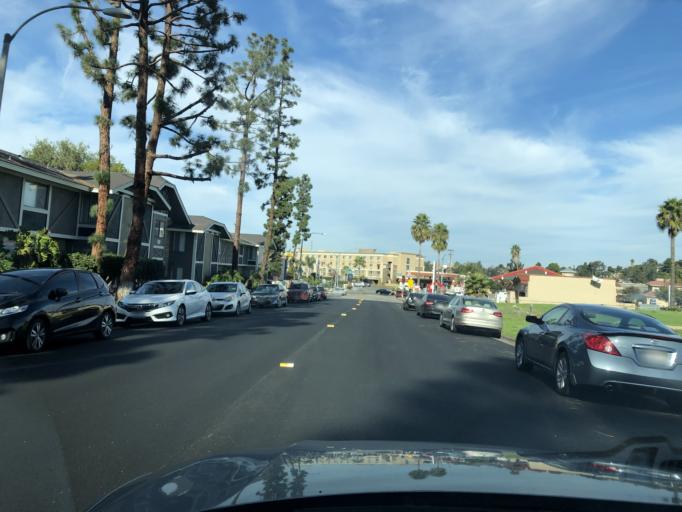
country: US
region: California
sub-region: San Diego County
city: Chula Vista
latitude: 32.6467
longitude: -117.0636
